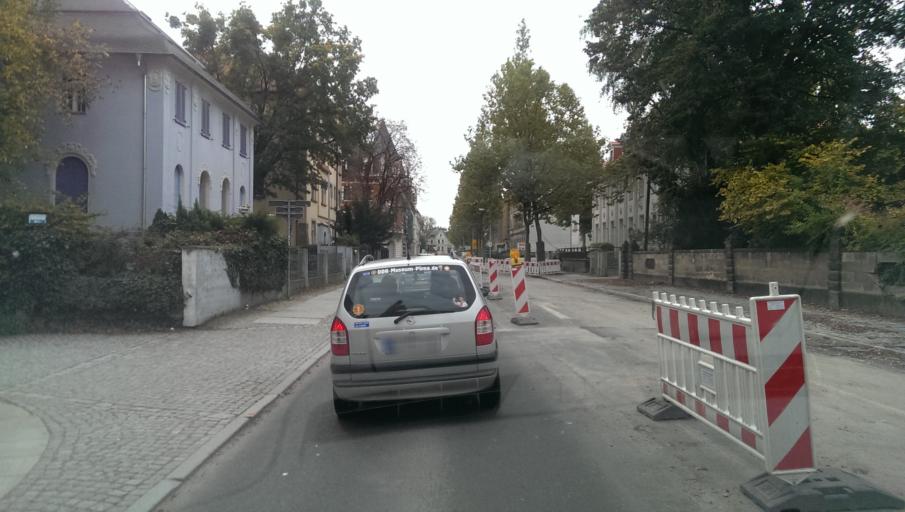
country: DE
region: Saxony
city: Pirna
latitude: 50.9602
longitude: 13.9311
